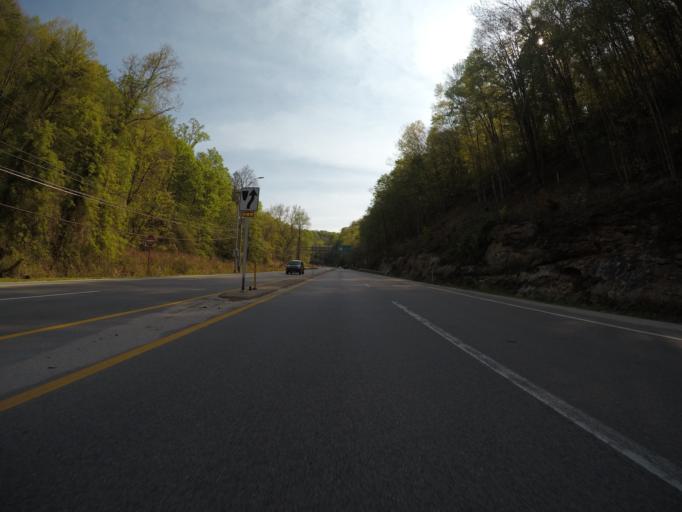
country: US
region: West Virginia
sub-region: Kanawha County
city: Charleston
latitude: 38.3576
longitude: -81.5955
